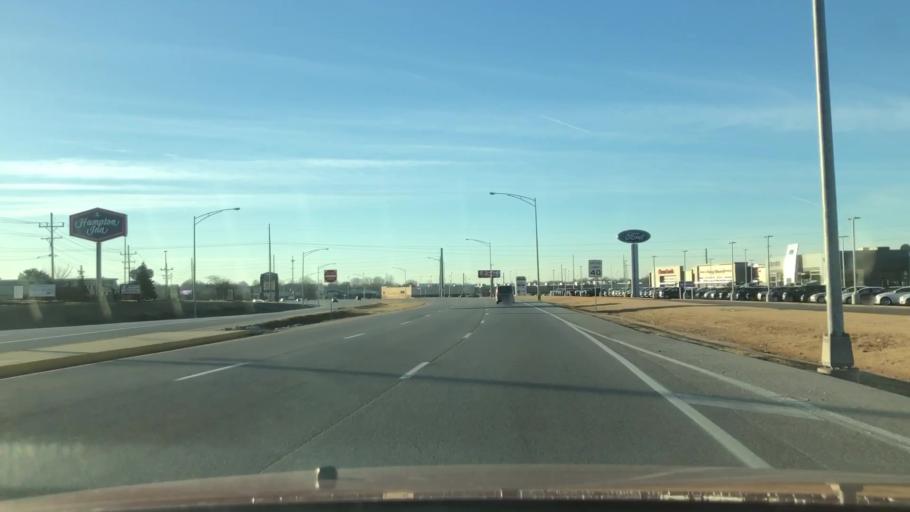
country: US
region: Missouri
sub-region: Greene County
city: Springfield
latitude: 37.1561
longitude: -93.2629
